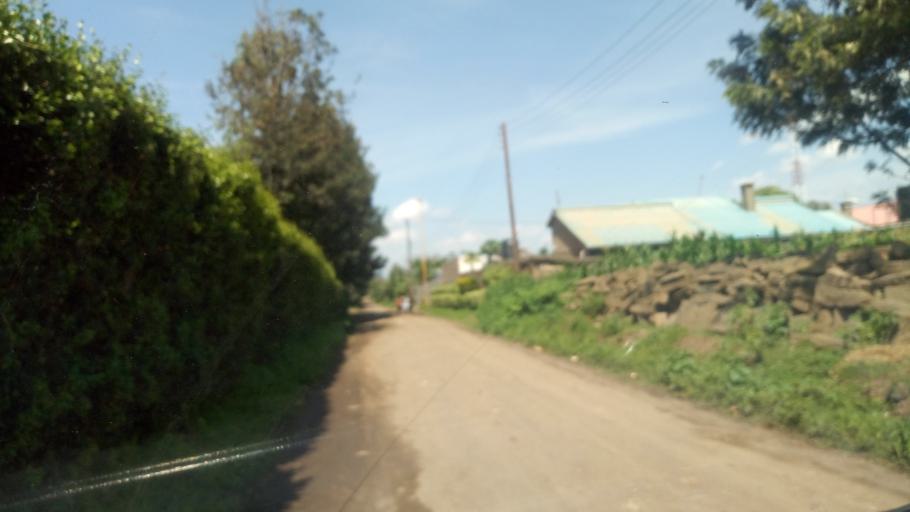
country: KE
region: Nakuru
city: Nakuru
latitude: -0.2764
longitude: 36.1133
